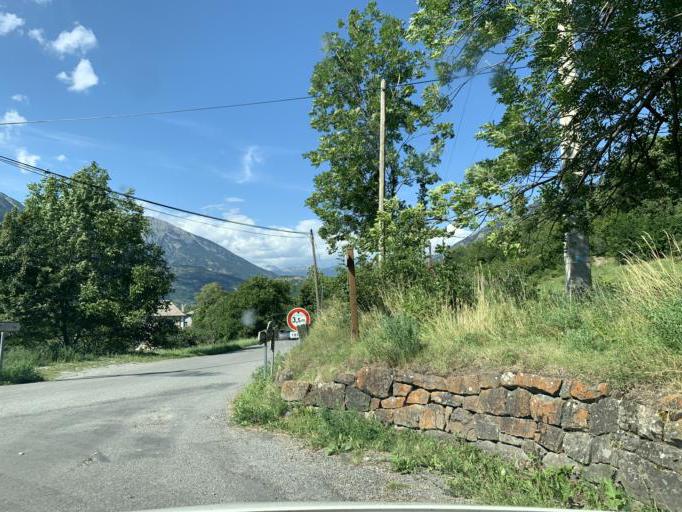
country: FR
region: Provence-Alpes-Cote d'Azur
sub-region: Departement des Hautes-Alpes
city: Embrun
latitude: 44.5872
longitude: 6.5333
